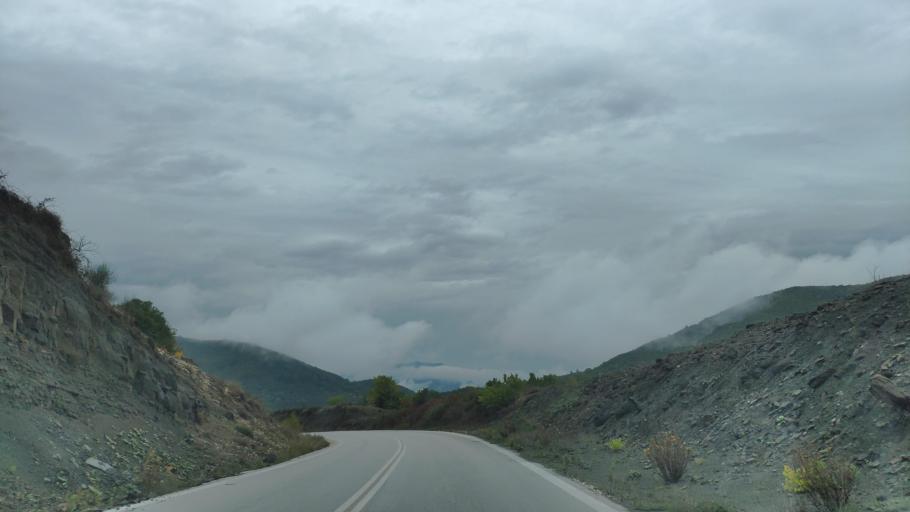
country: GR
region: Epirus
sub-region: Nomos Thesprotias
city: Paramythia
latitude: 39.4828
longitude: 20.6733
